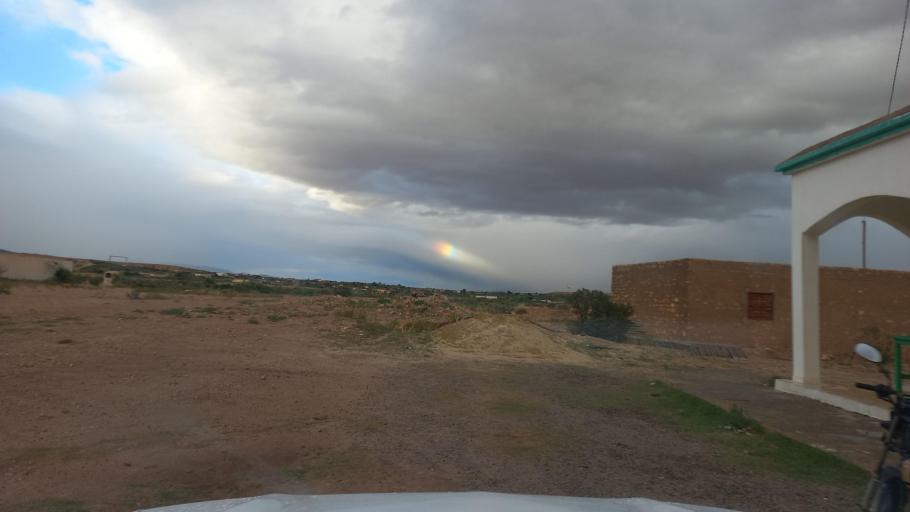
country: TN
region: Al Qasrayn
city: Kasserine
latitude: 35.2651
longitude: 8.9352
